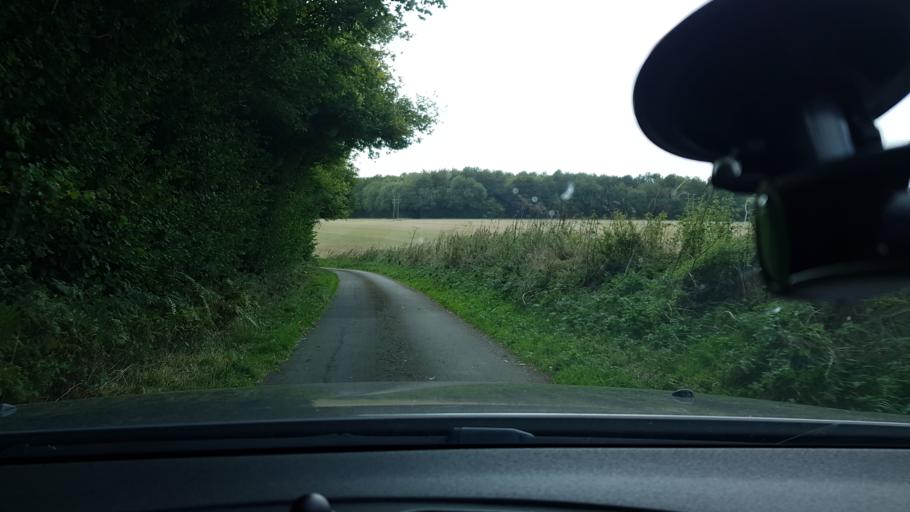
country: GB
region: England
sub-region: West Berkshire
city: Hungerford
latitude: 51.4541
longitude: -1.5036
